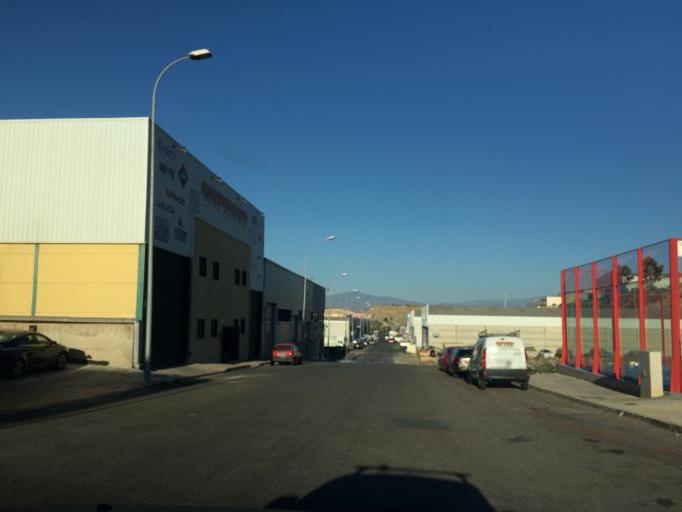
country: ES
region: Andalusia
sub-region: Provincia de Almeria
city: Viator
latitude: 36.8830
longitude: -2.4151
